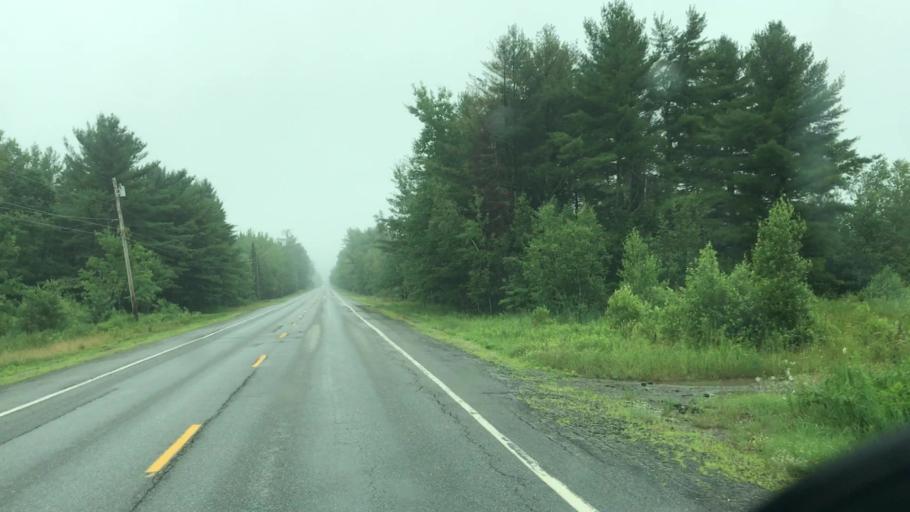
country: US
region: Maine
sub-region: Penobscot County
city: Howland
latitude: 45.2478
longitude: -68.6392
